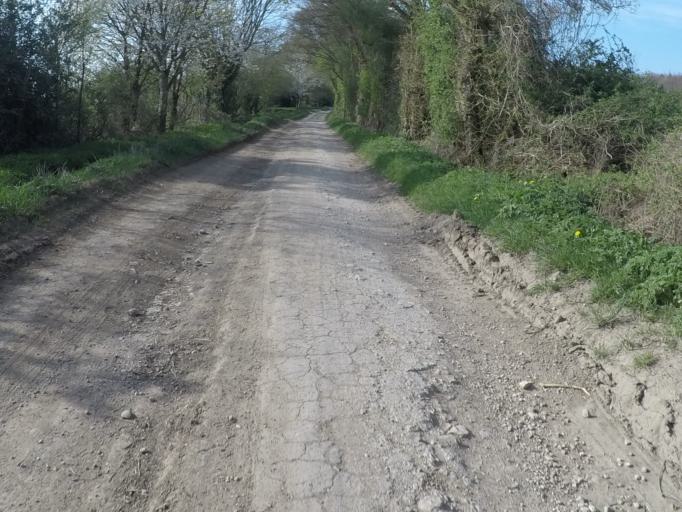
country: GB
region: England
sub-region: Oxfordshire
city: Charlbury
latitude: 51.8885
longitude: -1.4563
